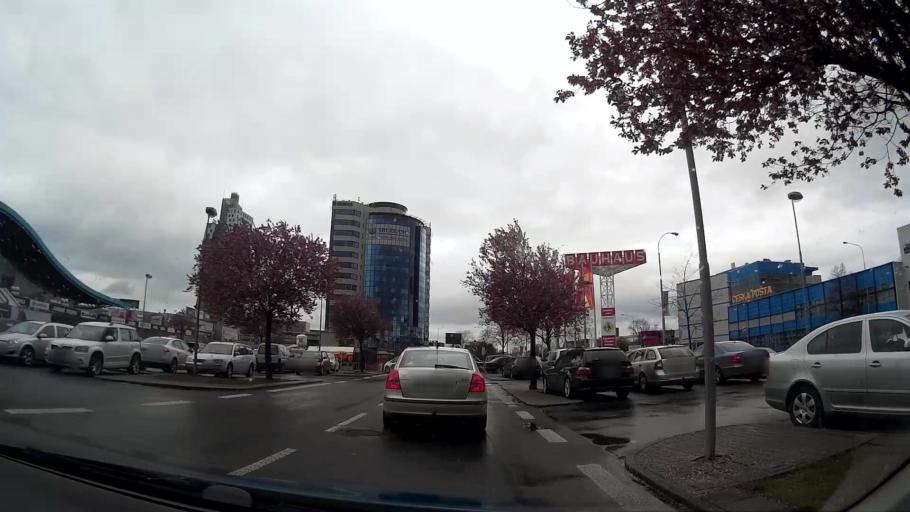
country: CZ
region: South Moravian
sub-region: Mesto Brno
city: Brno
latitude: 49.1789
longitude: 16.6044
